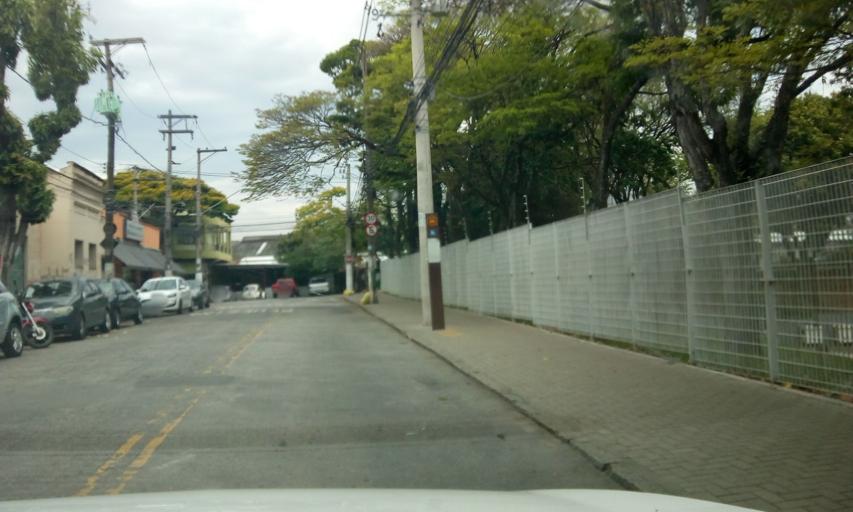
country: BR
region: Sao Paulo
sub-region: Sao Paulo
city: Sao Paulo
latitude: -23.5133
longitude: -46.7094
